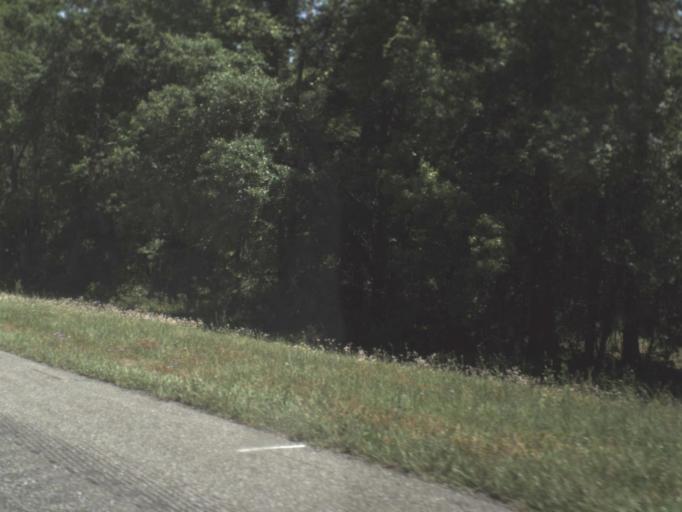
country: US
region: Florida
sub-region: Jefferson County
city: Monticello
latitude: 30.4728
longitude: -83.8501
